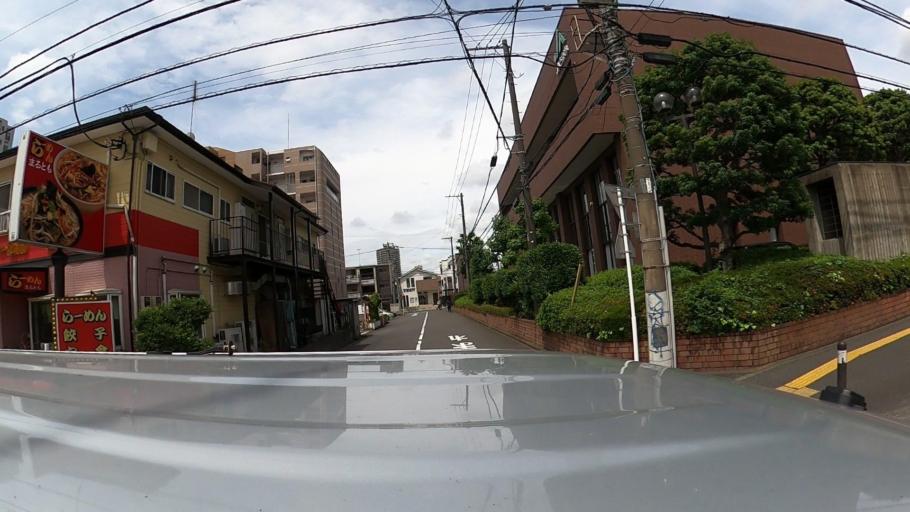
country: JP
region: Kanagawa
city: Fujisawa
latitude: 35.3998
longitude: 139.4696
